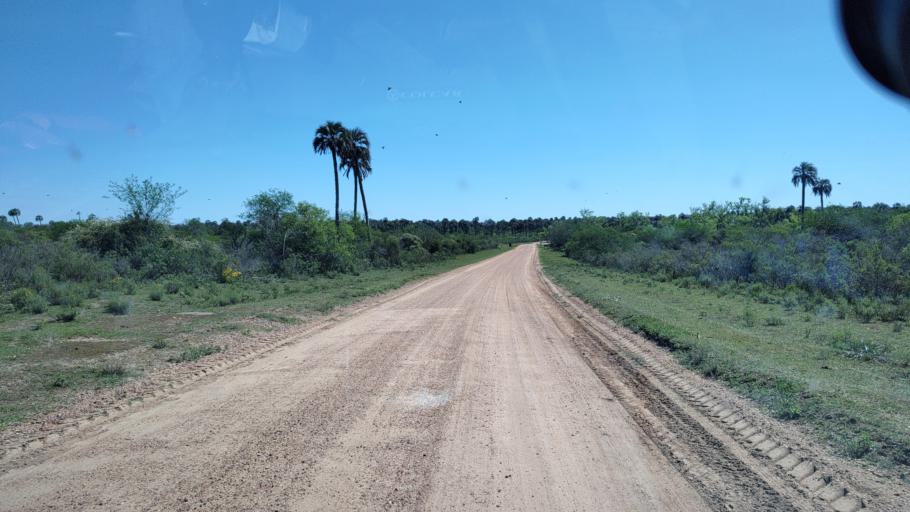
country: AR
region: Entre Rios
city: Ubajay
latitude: -31.8734
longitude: -58.2263
